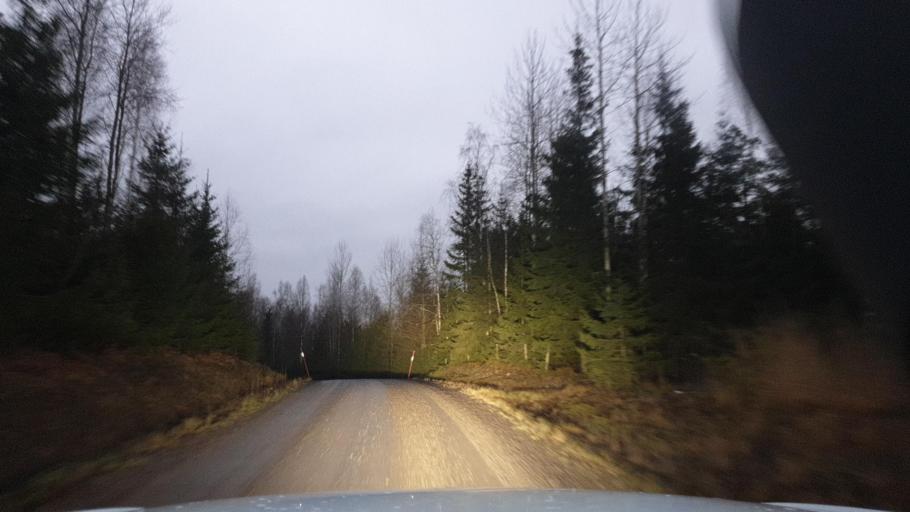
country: SE
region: Vaermland
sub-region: Eda Kommun
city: Amotfors
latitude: 59.8043
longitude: 12.4437
